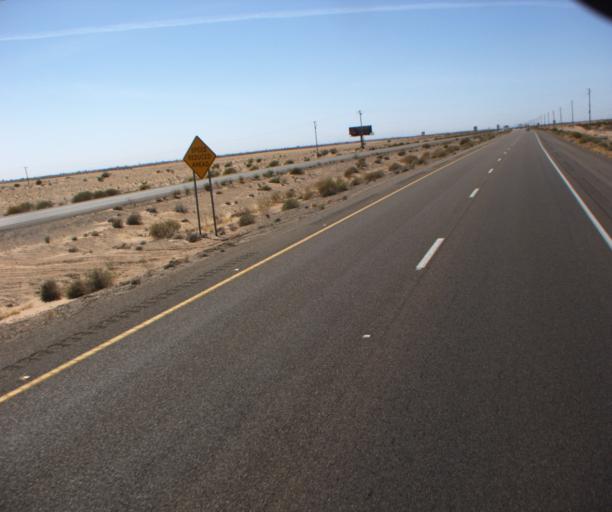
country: MX
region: Sonora
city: San Luis Rio Colorado
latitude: 32.4948
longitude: -114.6896
